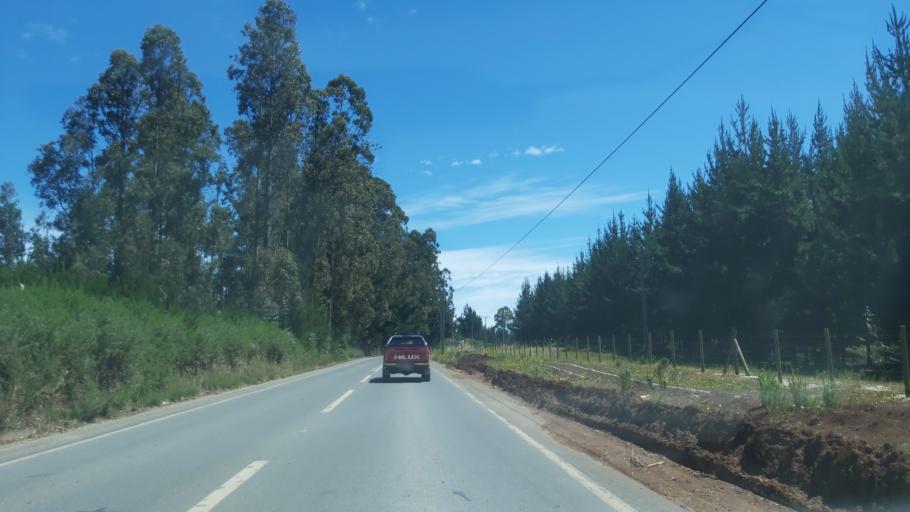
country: CL
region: Maule
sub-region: Provincia de Talca
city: Constitucion
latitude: -35.3962
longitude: -72.4304
